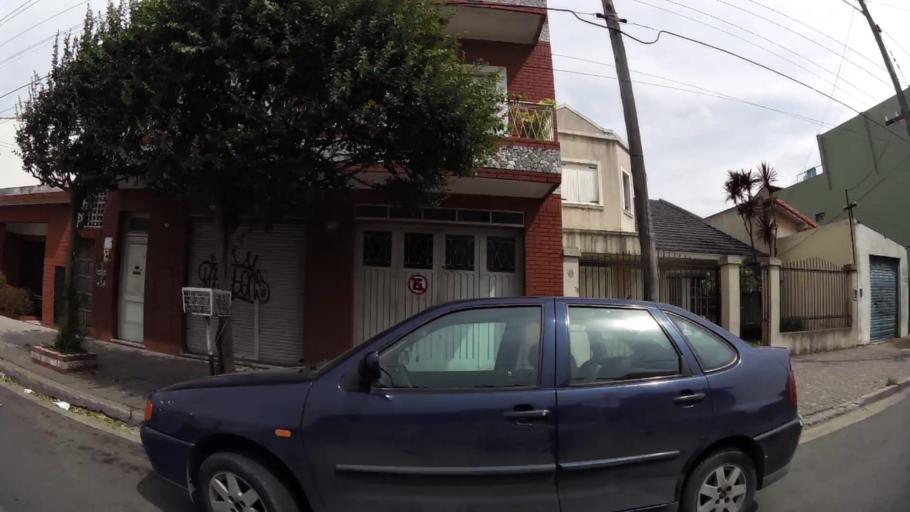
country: AR
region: Buenos Aires F.D.
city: Villa Lugano
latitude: -34.6930
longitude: -58.5107
